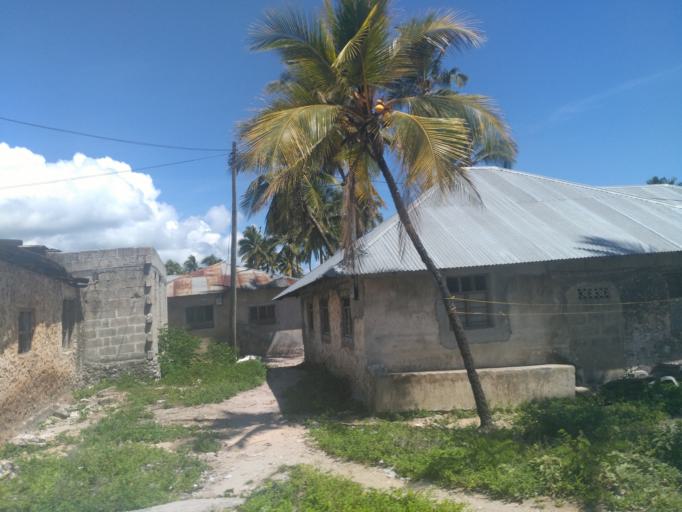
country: TZ
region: Zanzibar North
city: Gamba
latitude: -5.9242
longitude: 39.3569
